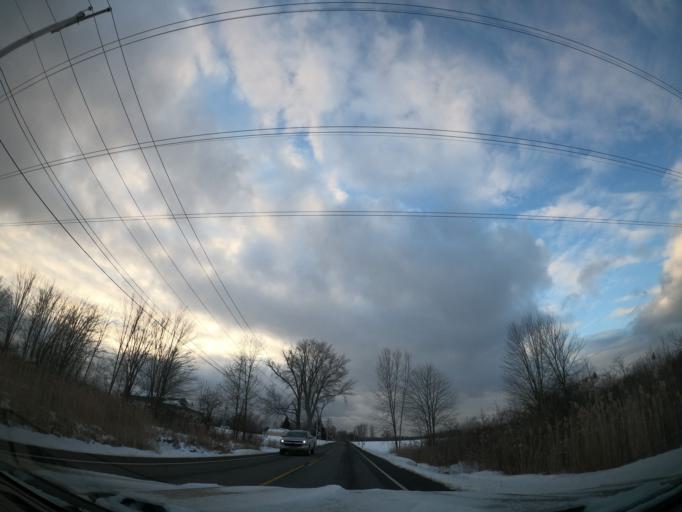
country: US
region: New York
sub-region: Onondaga County
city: Brewerton
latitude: 43.2013
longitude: -76.1726
